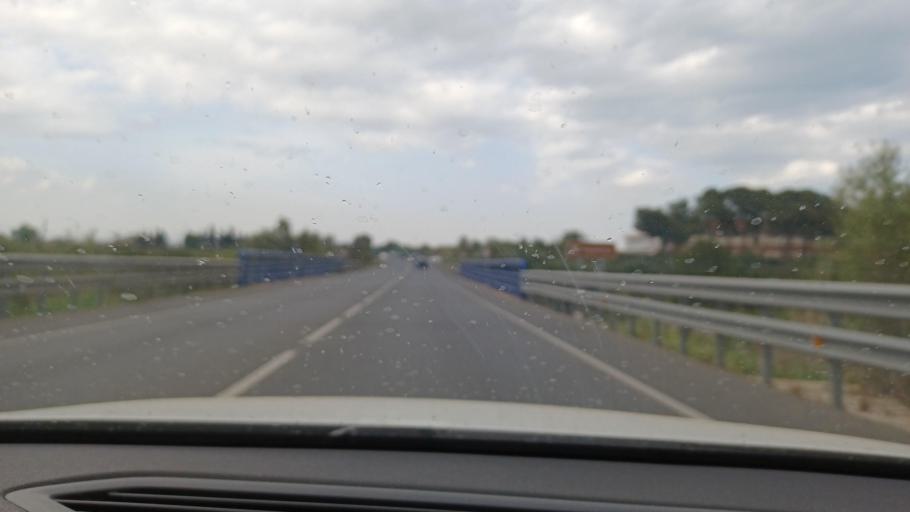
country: ES
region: Valencia
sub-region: Provincia de Castello
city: Benicarlo
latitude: 40.4463
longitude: 0.4481
